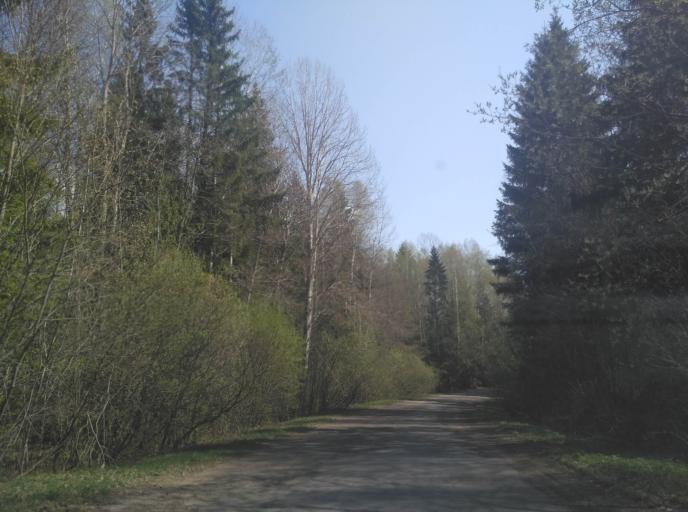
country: BY
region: Minsk
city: Loshnitsa
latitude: 54.4941
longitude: 28.7131
